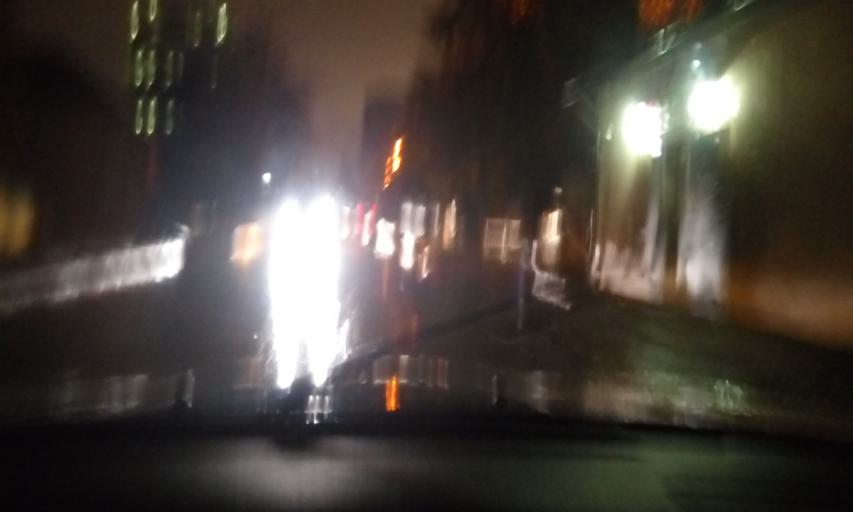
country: KZ
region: Astana Qalasy
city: Astana
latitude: 51.1377
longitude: 71.4280
